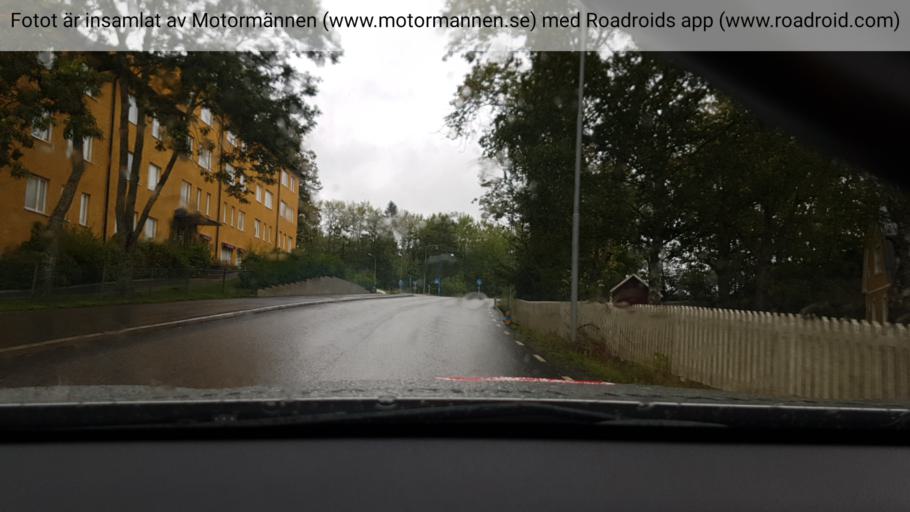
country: SE
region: Stockholm
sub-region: Haninge Kommun
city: Jordbro
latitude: 59.1034
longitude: 18.0468
